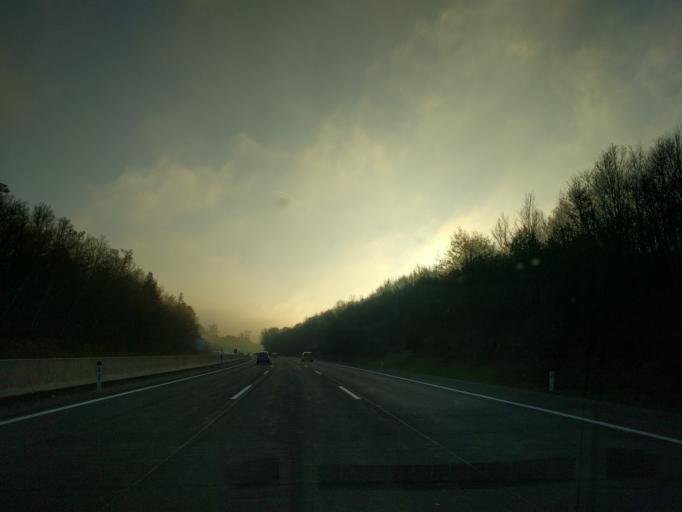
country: AT
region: Lower Austria
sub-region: Politischer Bezirk Wien-Umgebung
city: Purkersdorf
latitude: 48.1988
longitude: 16.2089
